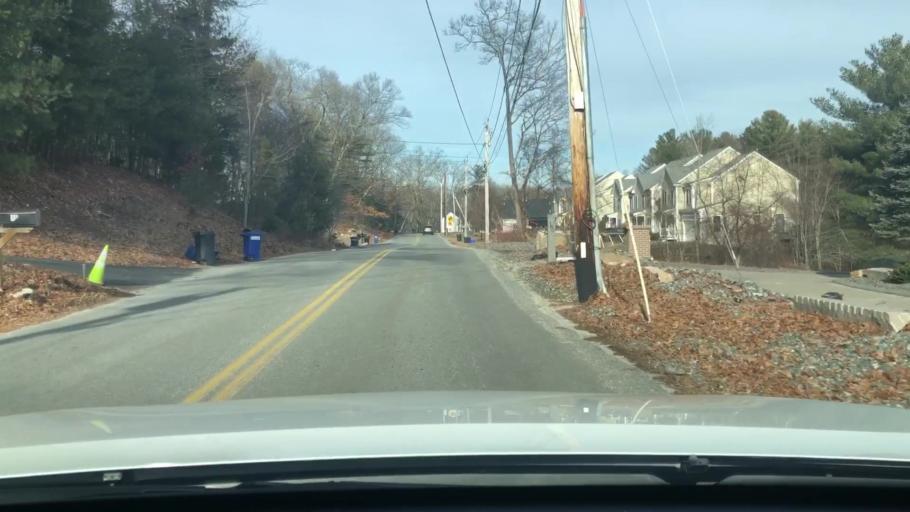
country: US
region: Massachusetts
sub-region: Worcester County
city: Milford
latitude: 42.1213
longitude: -71.4957
